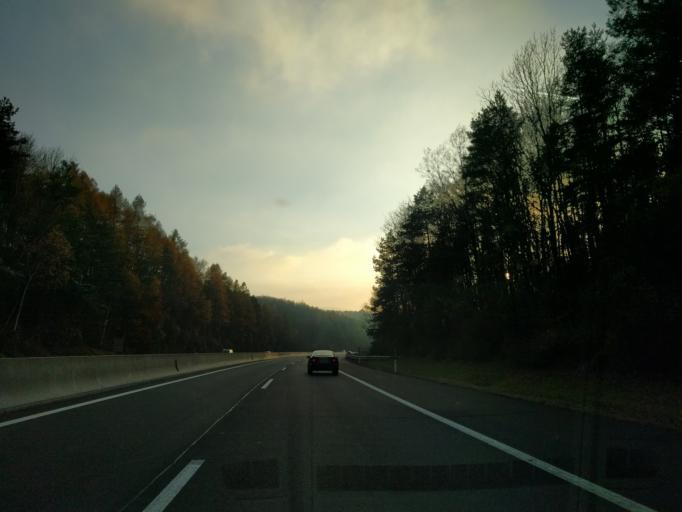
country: AT
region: Lower Austria
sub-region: Politischer Bezirk Sankt Polten
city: Eichgraben
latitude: 48.1574
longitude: 15.9902
